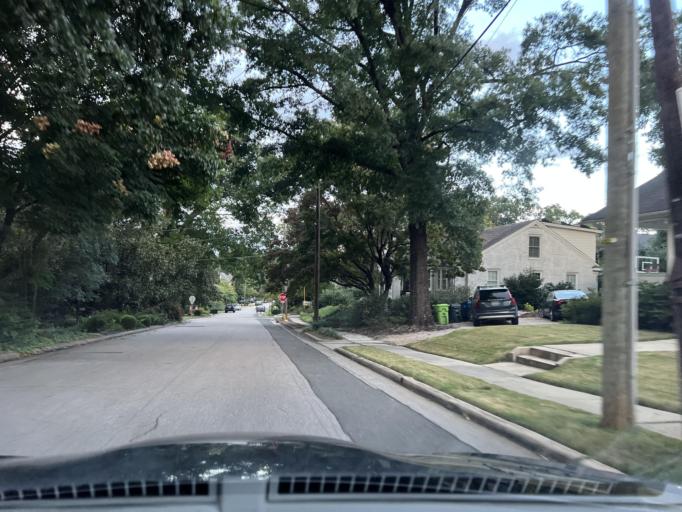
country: US
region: North Carolina
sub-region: Wake County
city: West Raleigh
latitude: 35.8120
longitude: -78.6496
